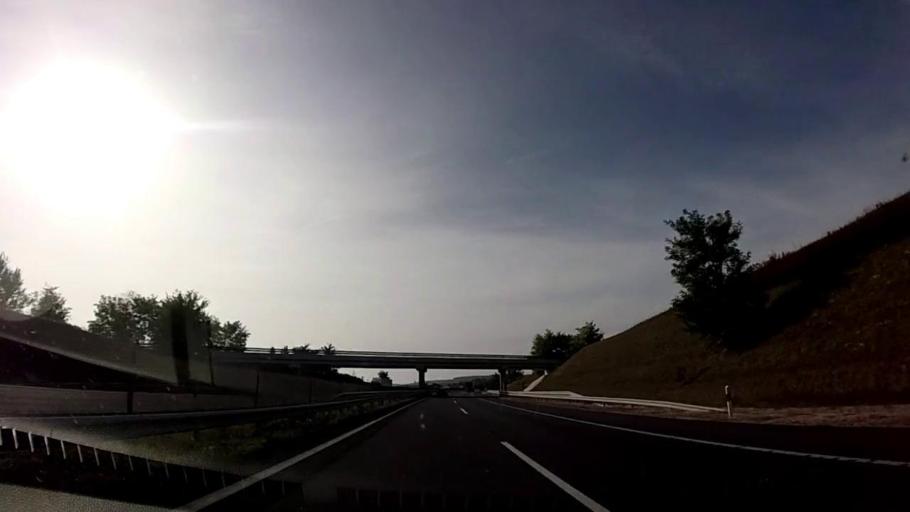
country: HU
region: Somogy
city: Zamardi
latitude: 46.8394
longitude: 17.9519
